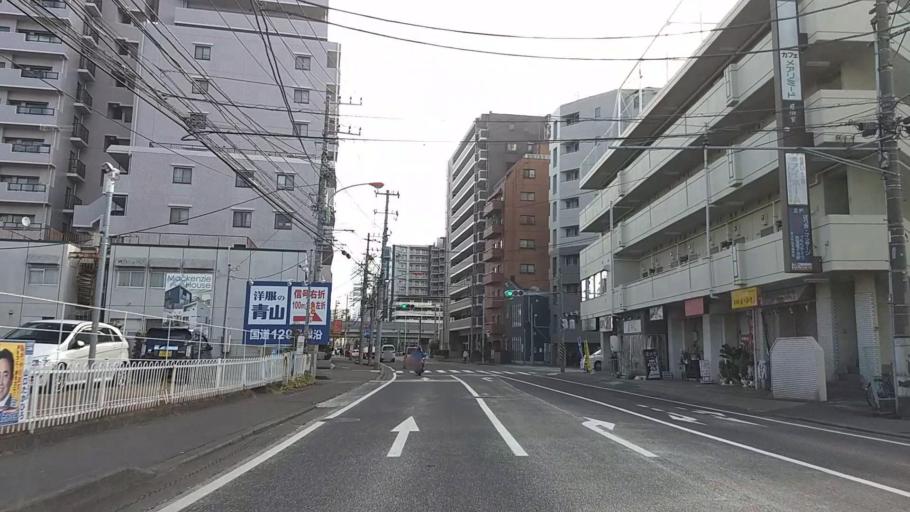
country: JP
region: Kanagawa
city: Atsugi
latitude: 35.4440
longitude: 139.3557
